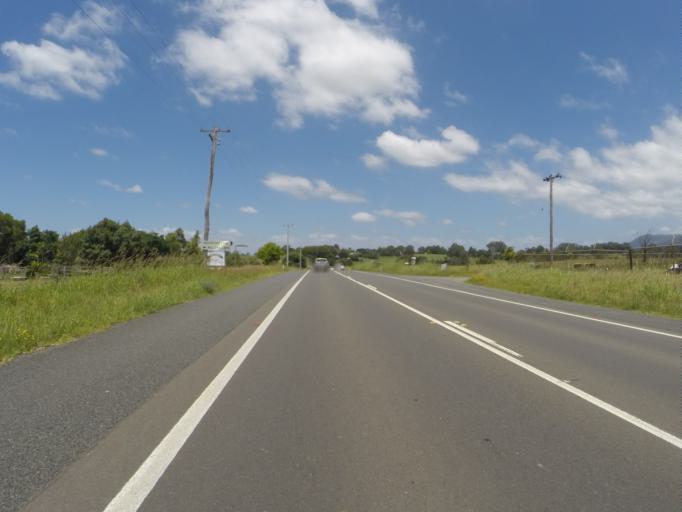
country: AU
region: New South Wales
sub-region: Shoalhaven Shire
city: Berry
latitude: -34.7865
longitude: 150.6754
